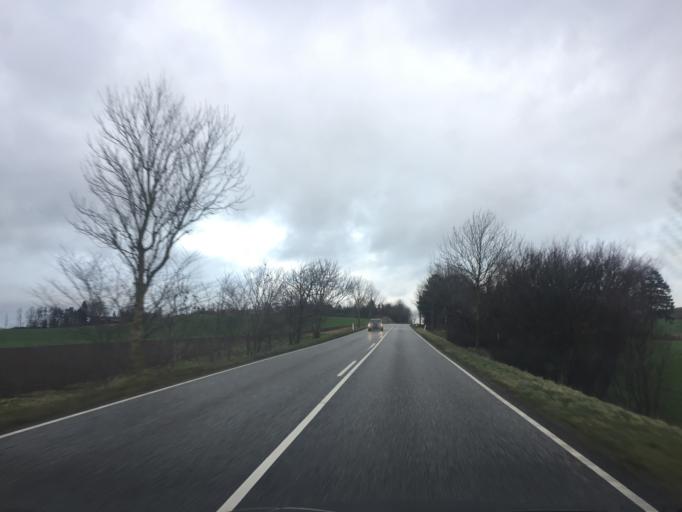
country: DK
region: Zealand
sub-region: Holbaek Kommune
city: Tollose
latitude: 55.6422
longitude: 11.8032
